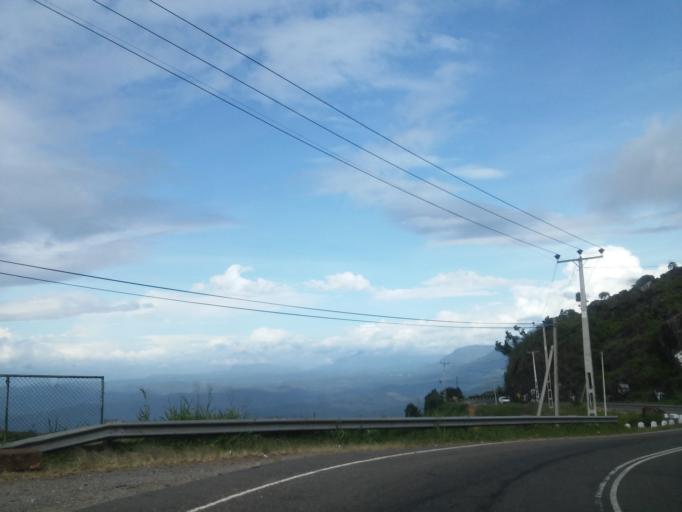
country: LK
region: Uva
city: Haputale
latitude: 6.7590
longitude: 80.9469
